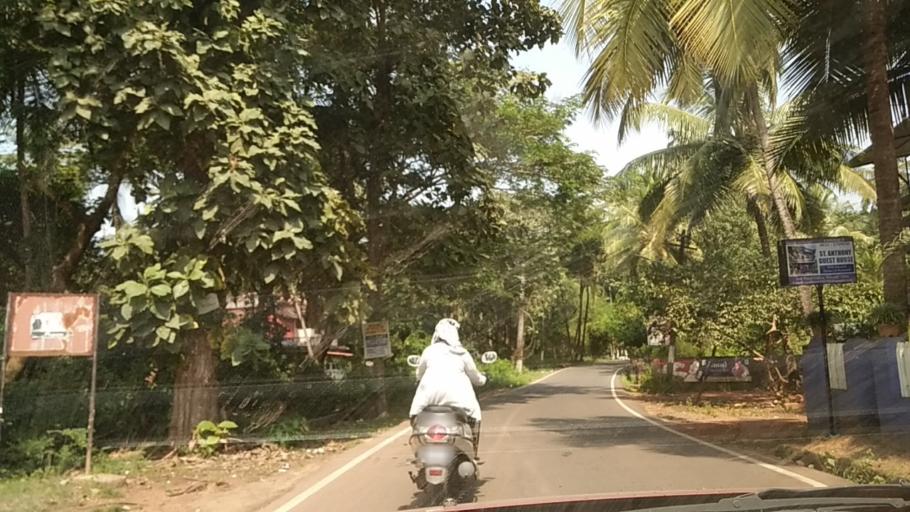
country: IN
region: Goa
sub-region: South Goa
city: Colva
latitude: 15.2850
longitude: 73.9203
